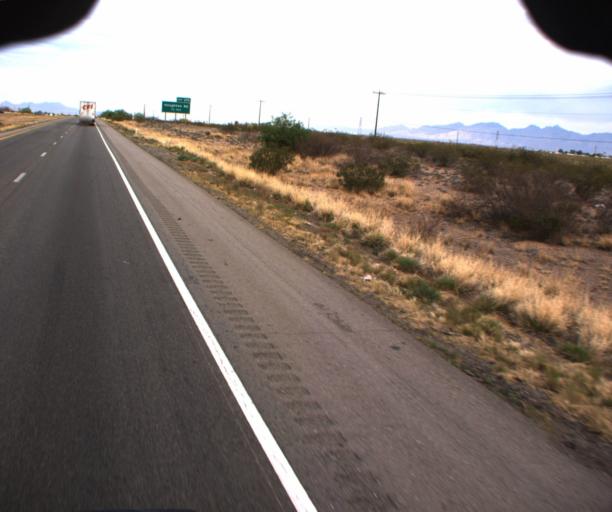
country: US
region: Arizona
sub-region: Pima County
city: Vail
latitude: 32.0545
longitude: -110.7622
